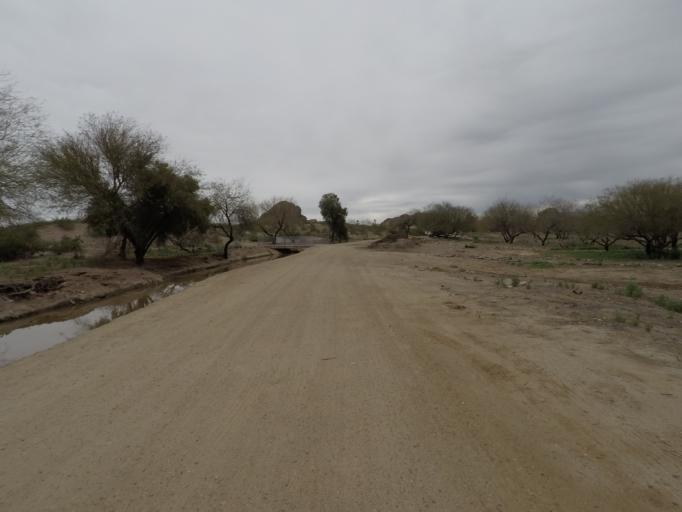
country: US
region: Arizona
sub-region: Maricopa County
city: Tempe Junction
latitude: 33.4362
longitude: -111.9347
